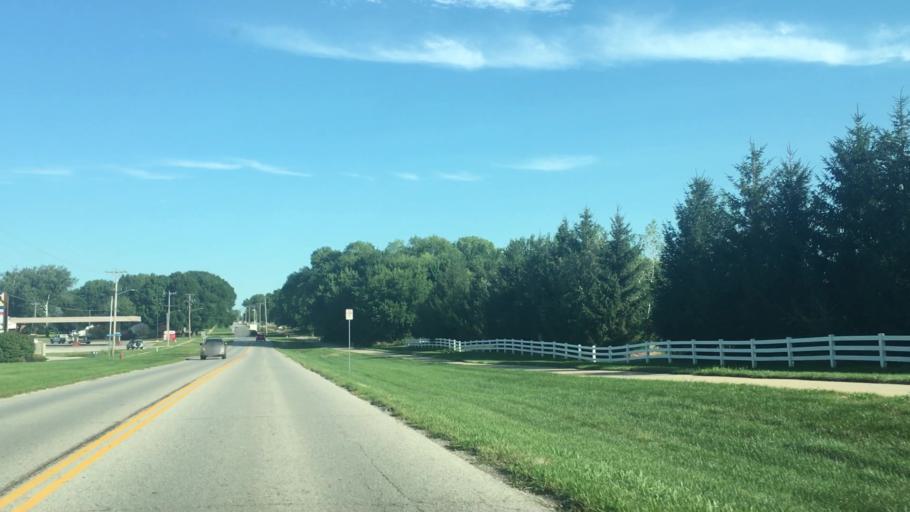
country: US
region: Iowa
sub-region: Johnson County
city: North Liberty
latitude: 41.7432
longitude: -91.5906
